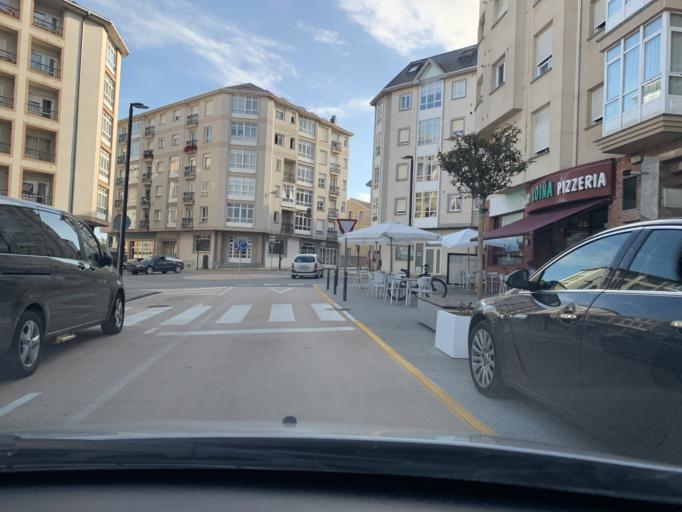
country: ES
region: Galicia
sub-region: Provincia de Lugo
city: Foz
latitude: 43.5658
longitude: -7.2621
